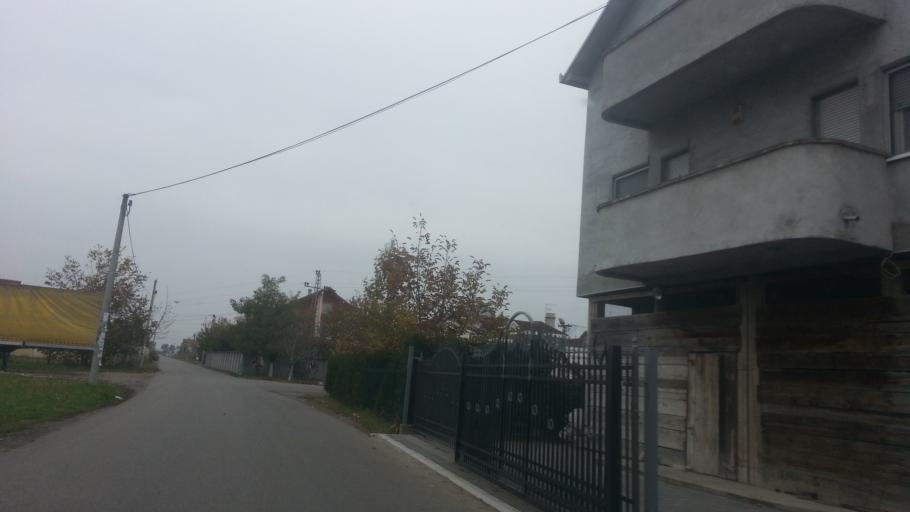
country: RS
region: Autonomna Pokrajina Vojvodina
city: Nova Pazova
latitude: 44.9518
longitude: 20.2089
